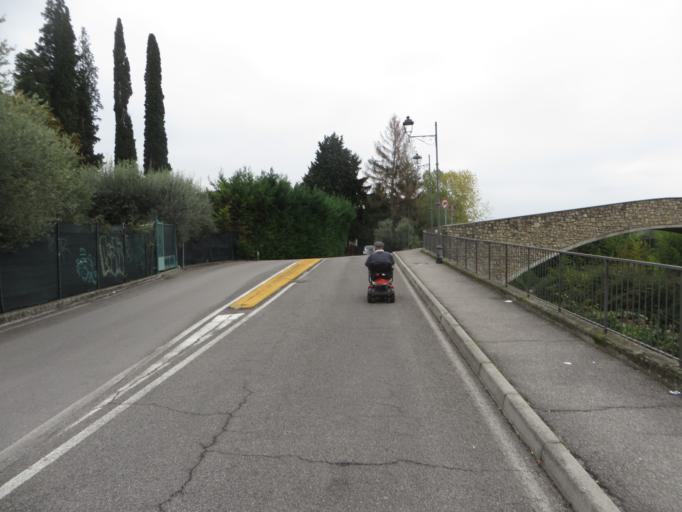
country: IT
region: Lombardy
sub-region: Provincia di Brescia
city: Toscolano Maderno
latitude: 45.6369
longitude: 10.6111
